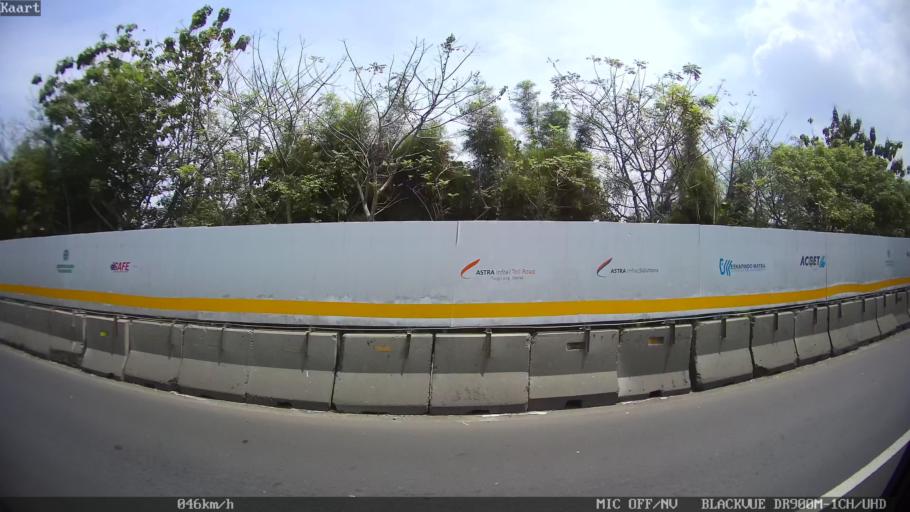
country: ID
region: Banten
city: Serang
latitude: -6.1295
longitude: 106.1963
